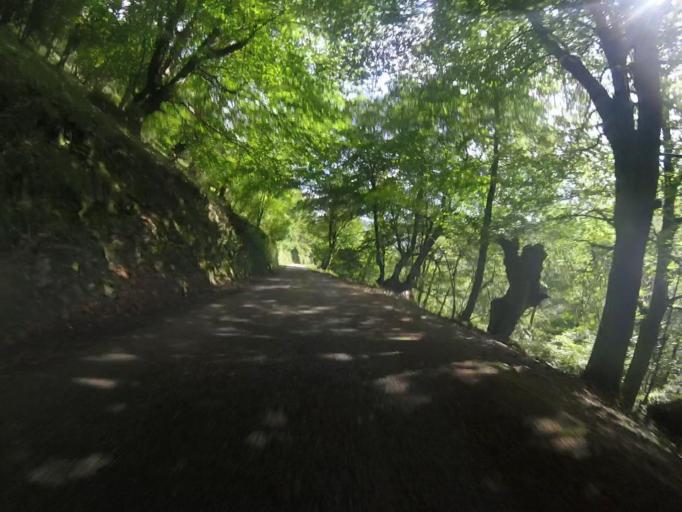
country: ES
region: Navarre
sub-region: Provincia de Navarra
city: Goizueta
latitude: 43.2193
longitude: -1.8056
